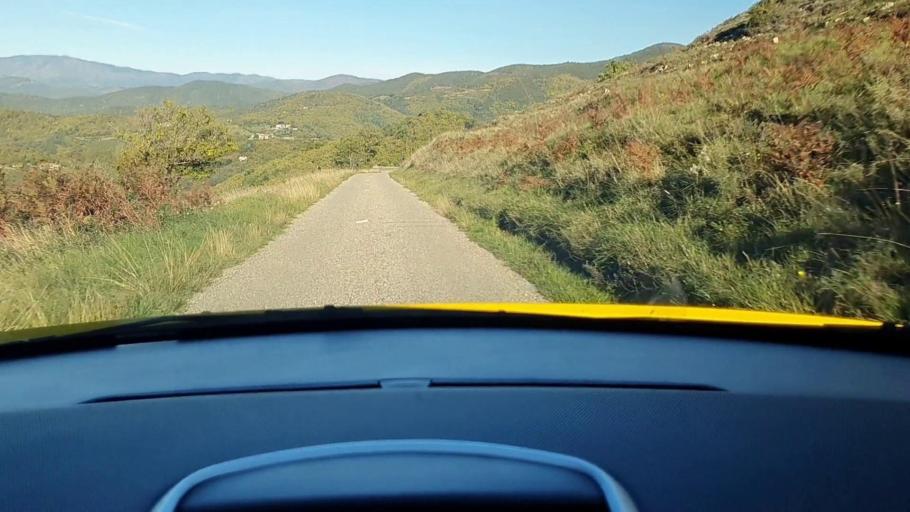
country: FR
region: Languedoc-Roussillon
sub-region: Departement du Gard
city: Sumene
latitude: 43.9805
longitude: 3.7484
